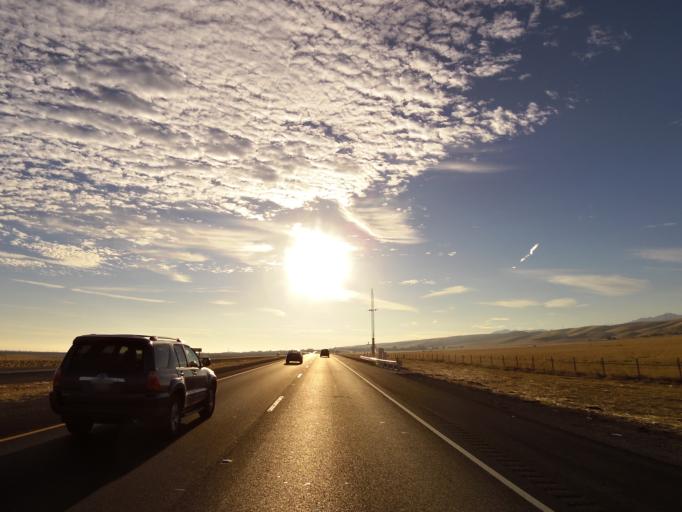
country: US
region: California
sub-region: San Joaquin County
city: Tracy
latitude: 37.6508
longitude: -121.4222
